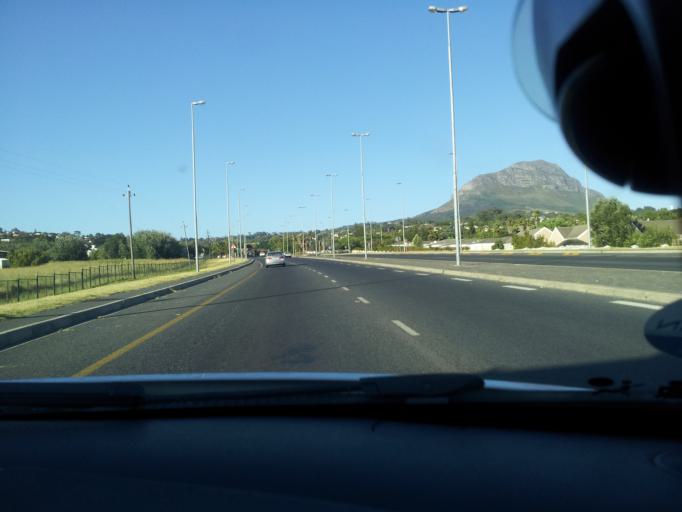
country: ZA
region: Western Cape
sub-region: Cape Winelands District Municipality
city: Stellenbosch
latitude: -34.0717
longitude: 18.8242
